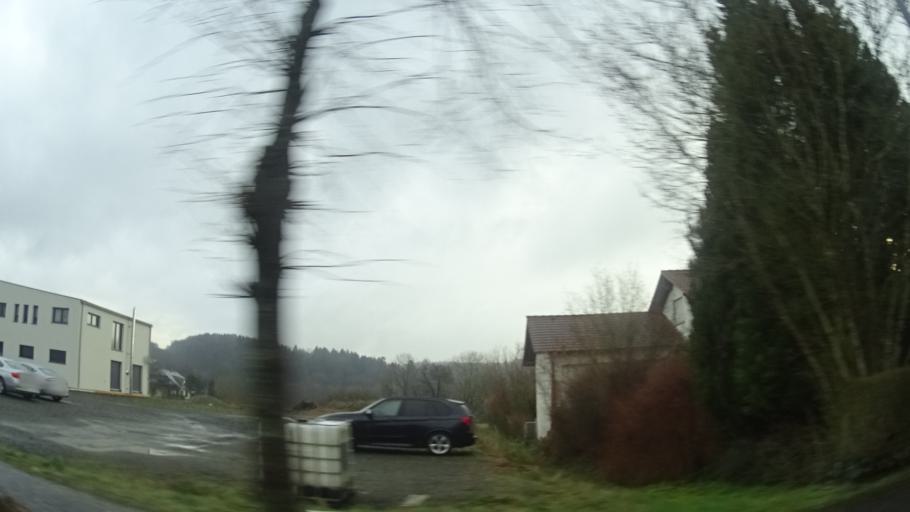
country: DE
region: Rheinland-Pfalz
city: Brucken
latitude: 49.6410
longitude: 7.1077
